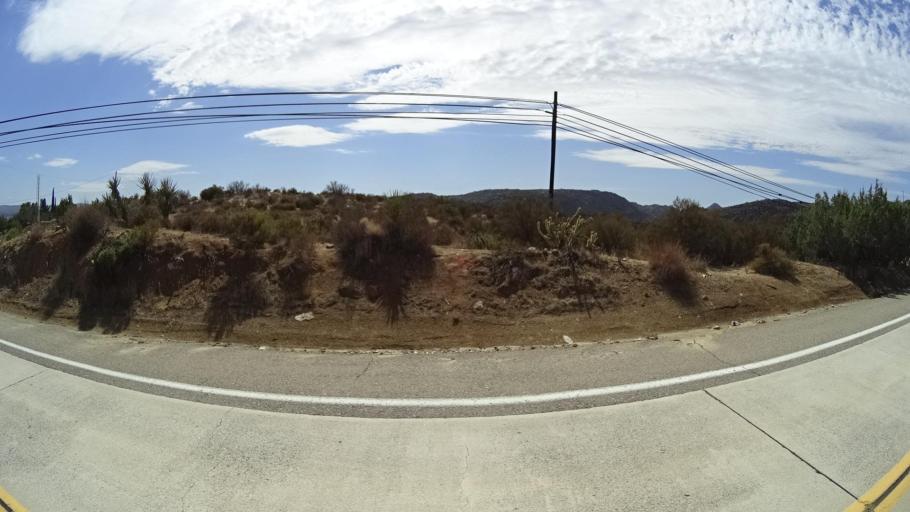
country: MX
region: Baja California
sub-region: Tecate
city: Cereso del Hongo
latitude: 32.6157
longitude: -116.2125
